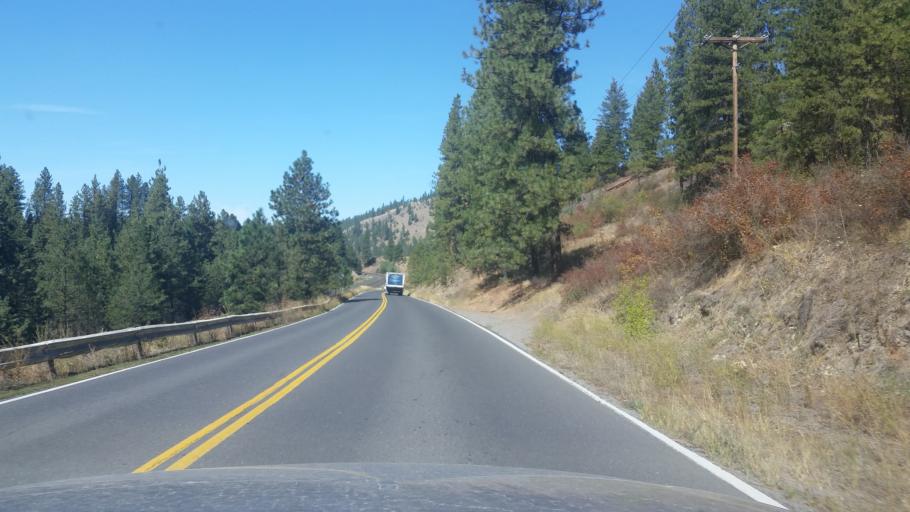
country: US
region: Washington
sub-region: Spokane County
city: Spokane
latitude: 47.6081
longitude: -117.4326
